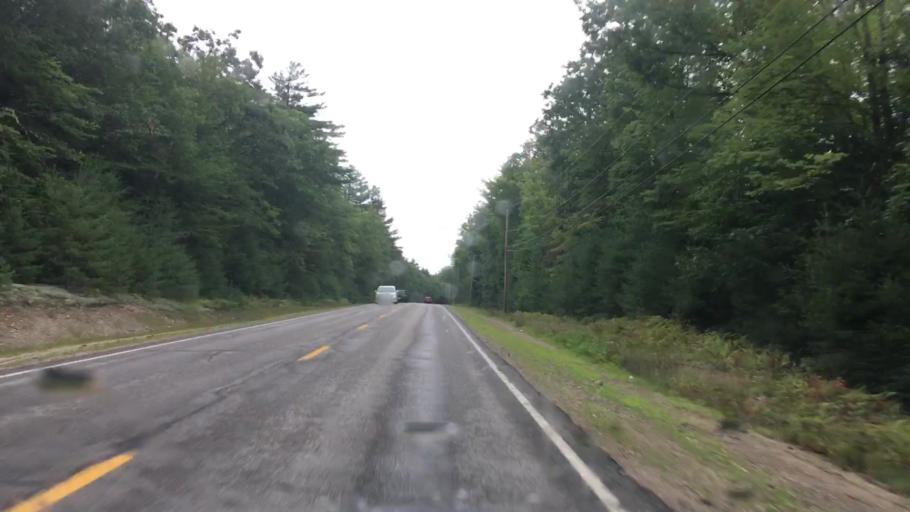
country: US
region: Maine
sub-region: Oxford County
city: Fryeburg
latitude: 43.9983
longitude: -70.9423
